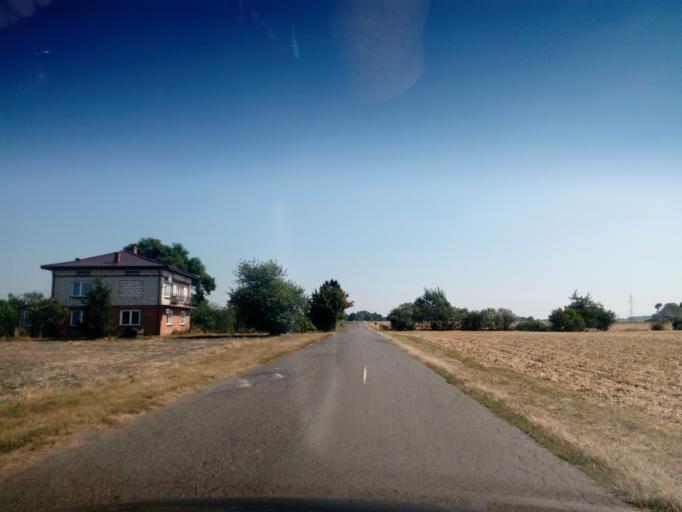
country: PL
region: Lublin Voivodeship
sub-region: Powiat hrubieszowski
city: Hrubieszow
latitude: 50.7298
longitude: 23.9103
